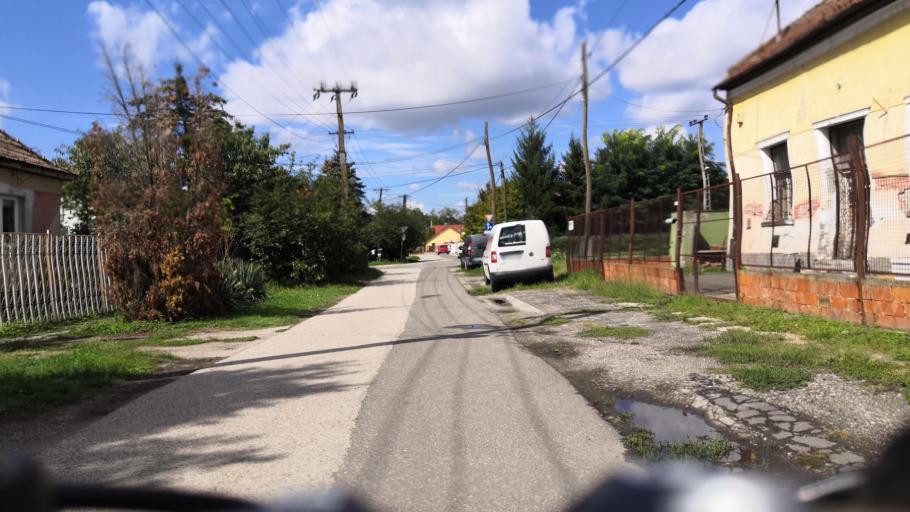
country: HU
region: Csongrad
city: Szeged
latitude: 46.2774
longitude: 20.1219
